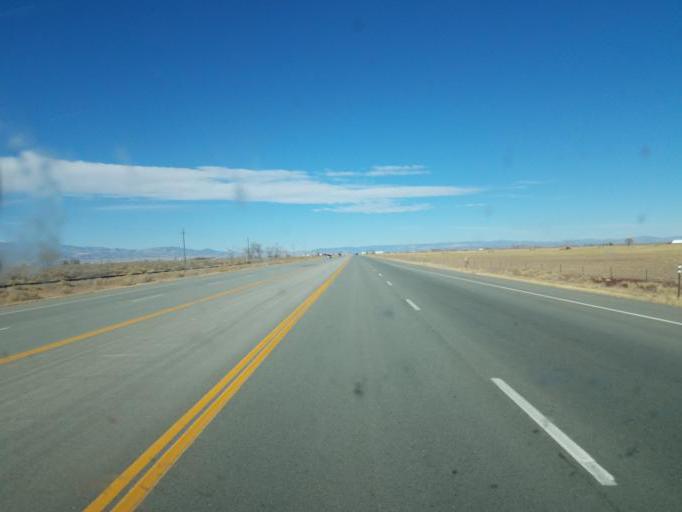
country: US
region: Colorado
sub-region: Alamosa County
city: Alamosa
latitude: 37.5227
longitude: -106.0066
